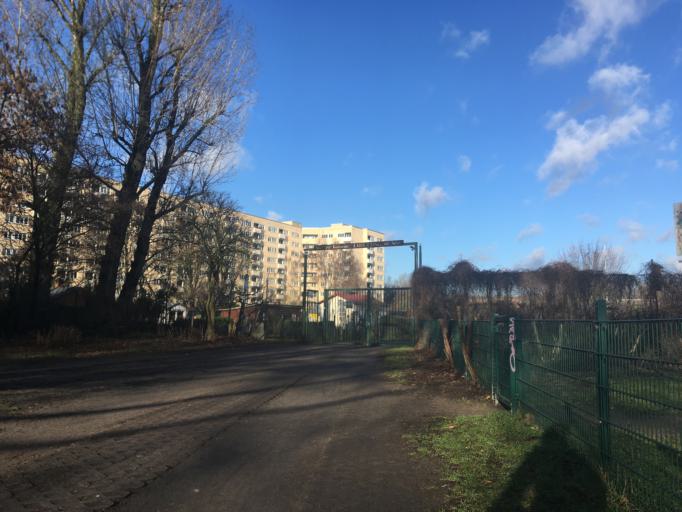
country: DE
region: Berlin
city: Reinickendorf
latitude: 52.5711
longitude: 13.3240
